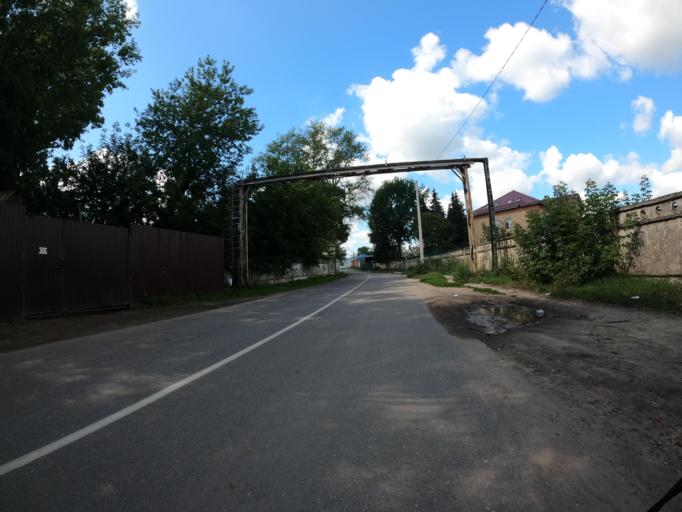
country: RU
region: Moskovskaya
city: Lopatinskiy
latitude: 55.3133
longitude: 38.6951
